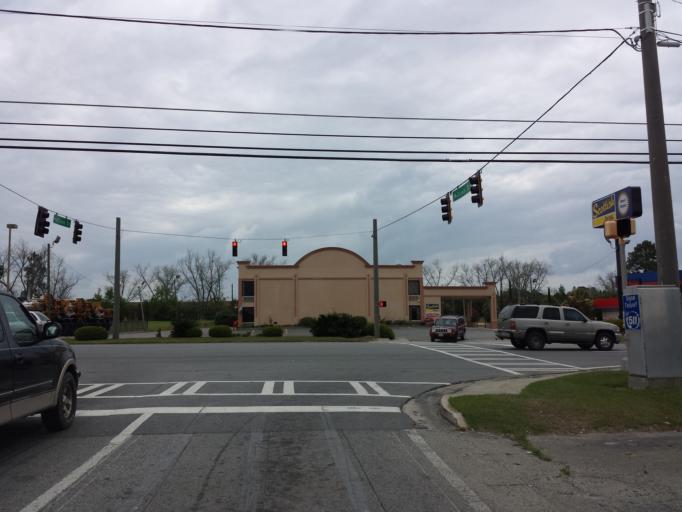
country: US
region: Georgia
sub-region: Tift County
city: Tifton
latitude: 31.4480
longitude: -83.5367
